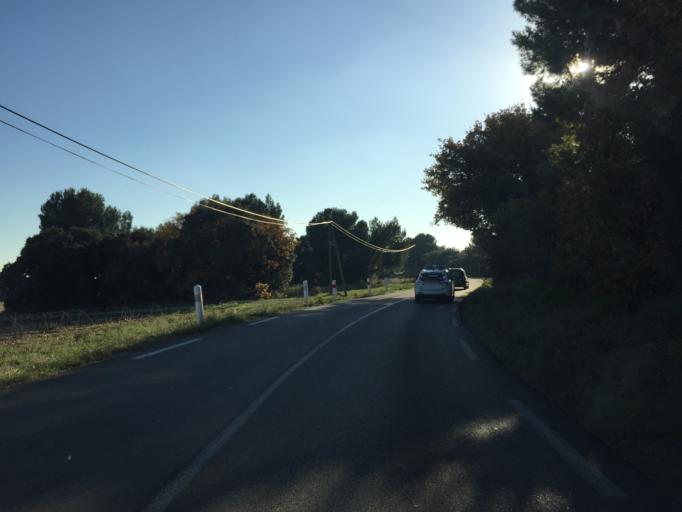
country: FR
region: Provence-Alpes-Cote d'Azur
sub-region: Departement du Vaucluse
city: Serignan-du-Comtat
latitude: 44.1999
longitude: 4.8670
